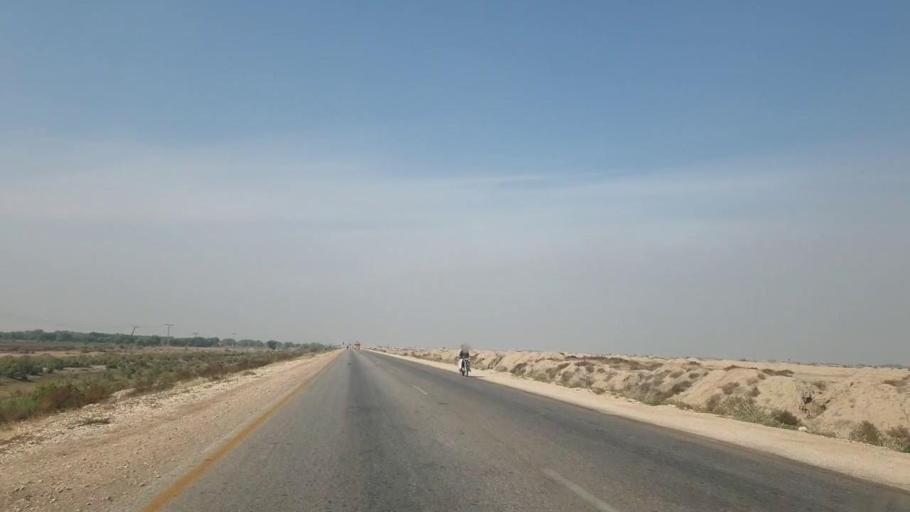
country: PK
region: Sindh
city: Sann
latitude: 25.9360
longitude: 68.2066
